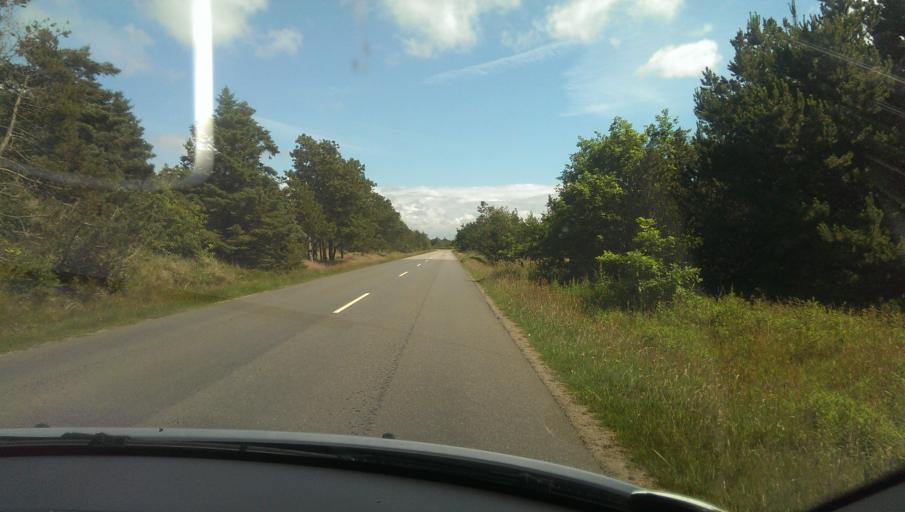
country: DK
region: Central Jutland
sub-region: Ringkobing-Skjern Kommune
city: Ringkobing
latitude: 56.1424
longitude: 8.1450
